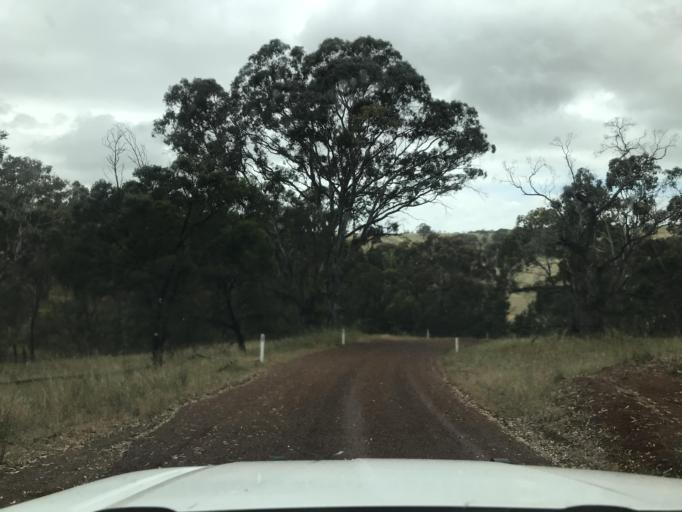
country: AU
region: South Australia
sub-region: Wattle Range
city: Penola
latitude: -37.2335
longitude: 141.4578
